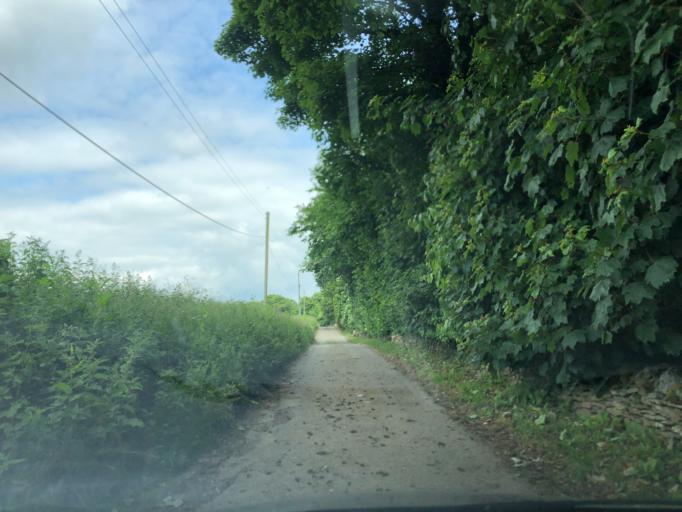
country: GB
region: England
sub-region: North Yorkshire
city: Helmsley
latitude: 54.1580
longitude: -1.0048
